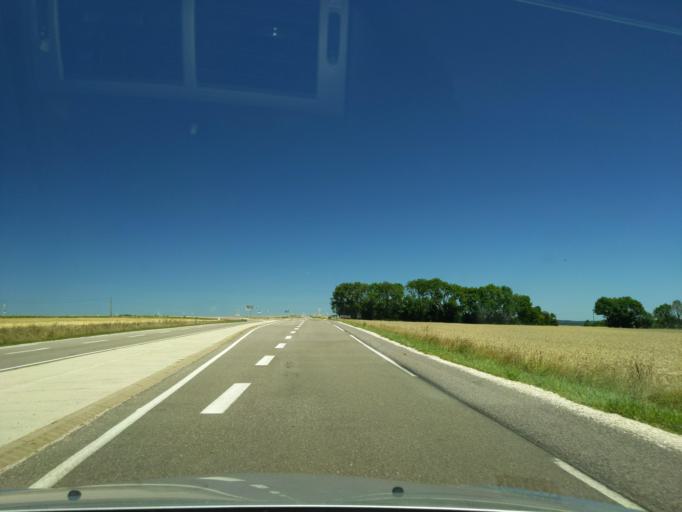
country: FR
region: Bourgogne
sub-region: Departement de la Cote-d'Or
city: Is-sur-Tille
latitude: 47.4946
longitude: 5.0919
